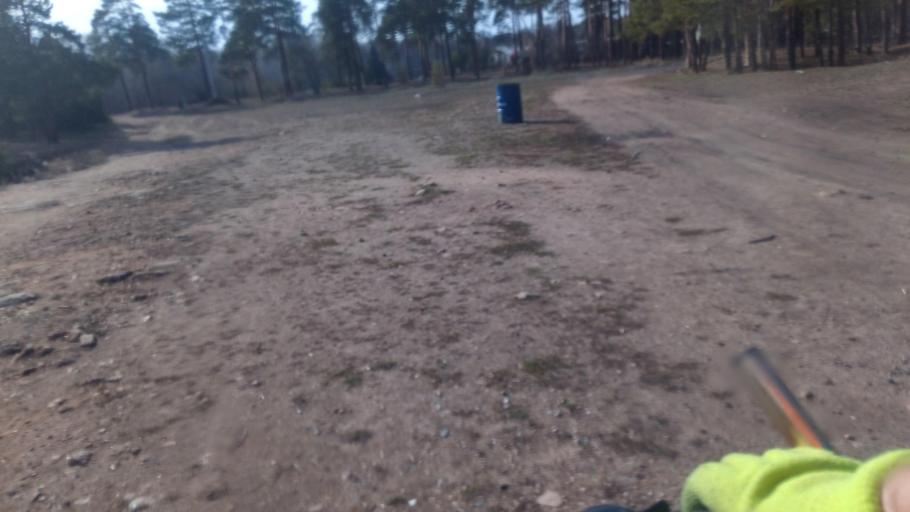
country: RU
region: Chelyabinsk
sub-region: Gorod Chelyabinsk
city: Chelyabinsk
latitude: 55.1539
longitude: 61.3367
